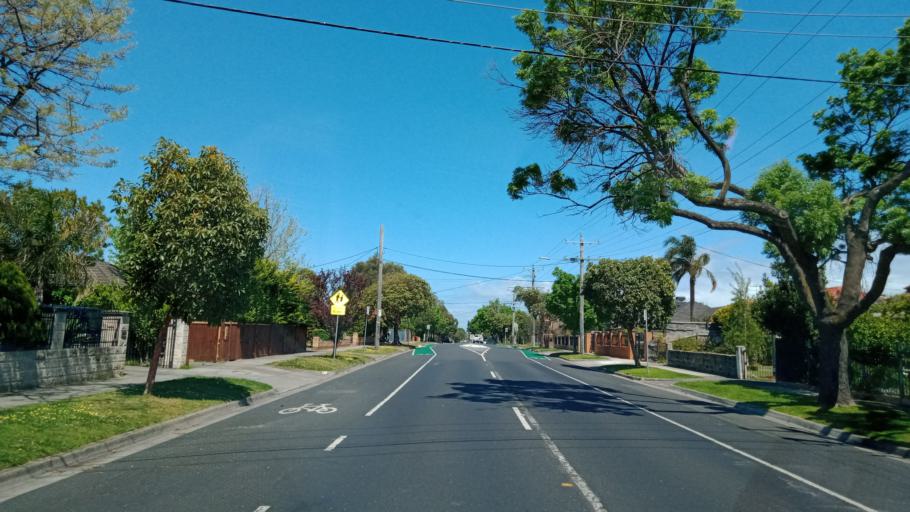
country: AU
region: Victoria
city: McKinnon
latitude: -37.9223
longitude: 145.0505
